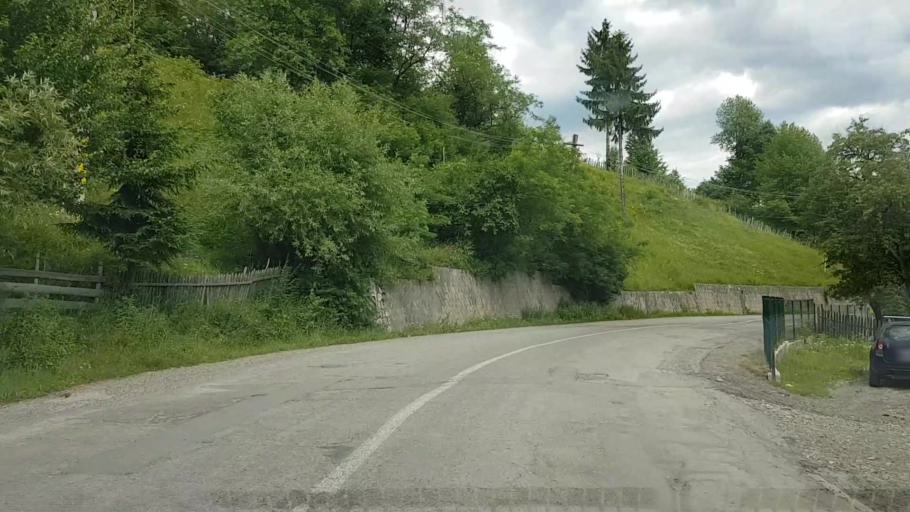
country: RO
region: Neamt
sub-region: Comuna Hangu
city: Hangu
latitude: 47.0539
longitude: 26.0247
